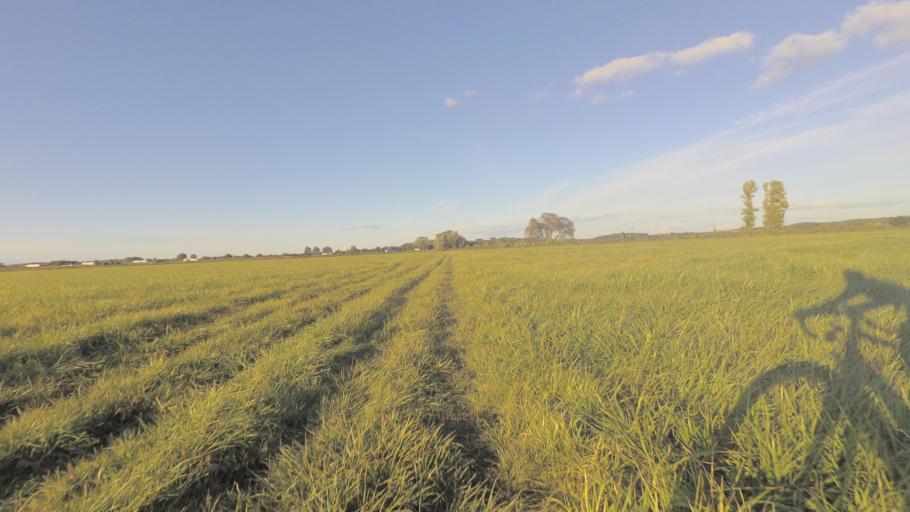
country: DE
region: Brandenburg
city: Rangsdorf
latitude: 52.3015
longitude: 13.3568
